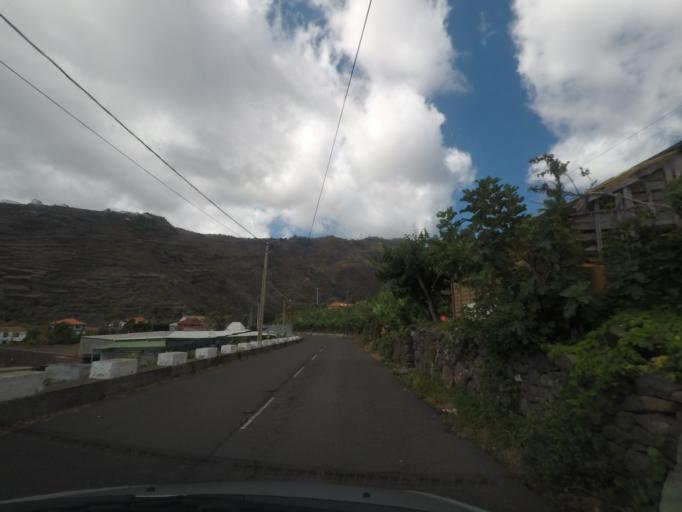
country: PT
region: Madeira
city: Ponta do Sol
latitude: 32.6807
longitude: -17.0727
